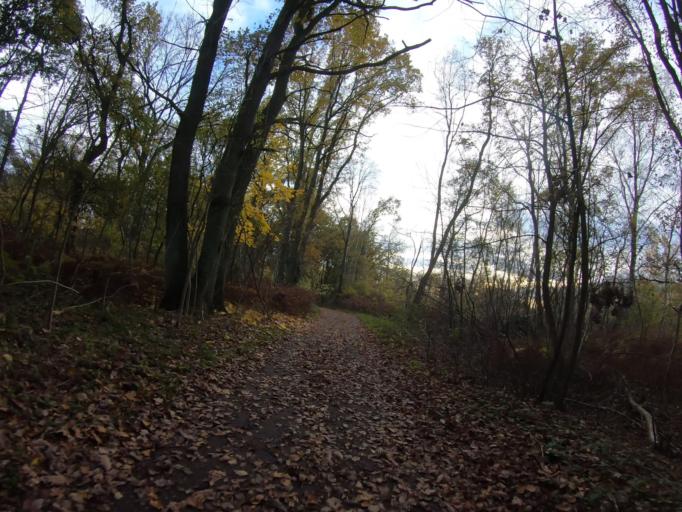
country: DE
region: Lower Saxony
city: Gifhorn
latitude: 52.4747
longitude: 10.5199
